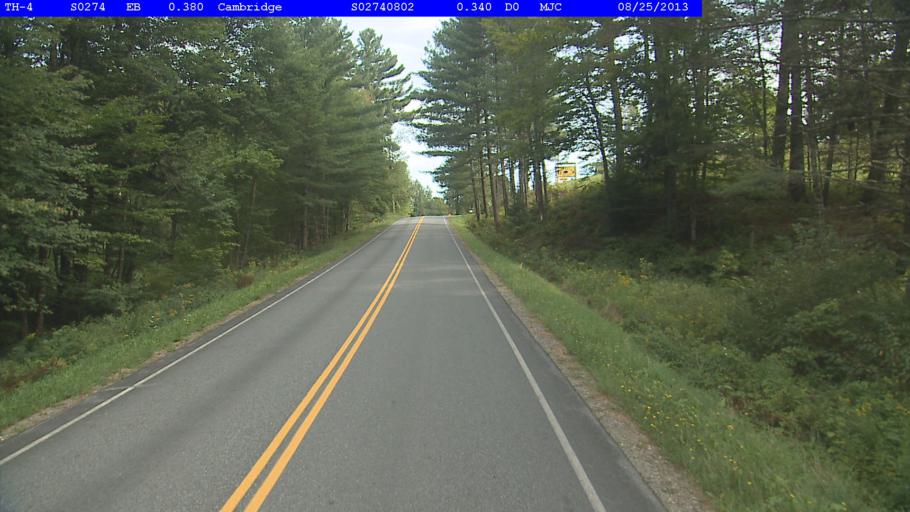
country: US
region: Vermont
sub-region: Lamoille County
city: Johnson
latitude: 44.6777
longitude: -72.7706
